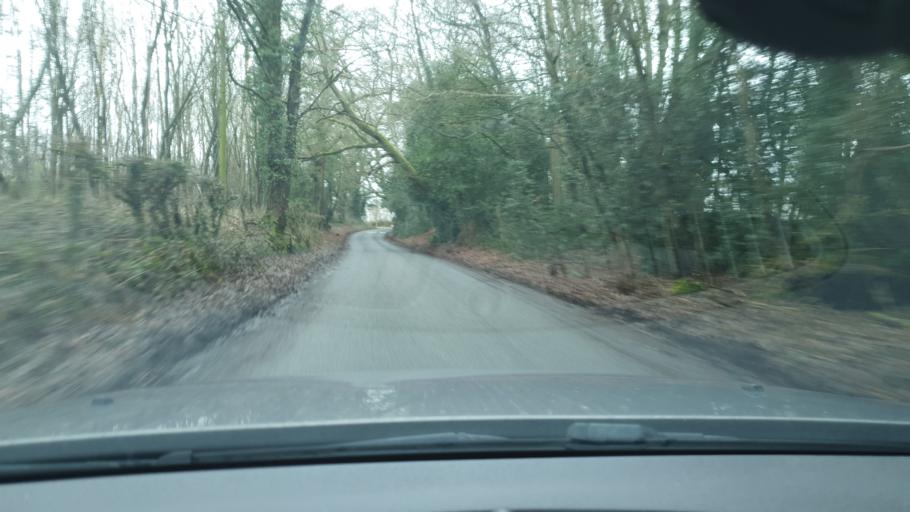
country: GB
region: England
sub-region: West Berkshire
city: Greenham
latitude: 51.3674
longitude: -1.2996
